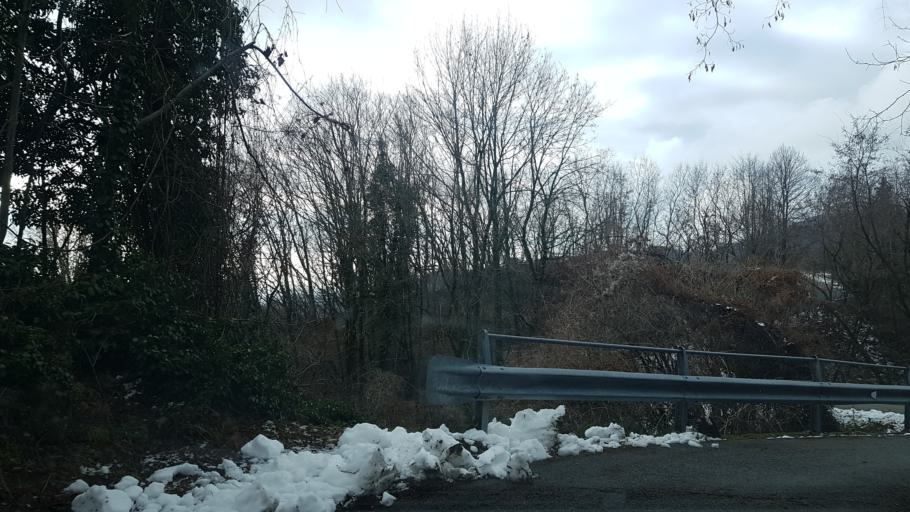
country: IT
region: Friuli Venezia Giulia
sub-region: Provincia di Udine
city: Savogna
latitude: 46.1730
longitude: 13.5496
